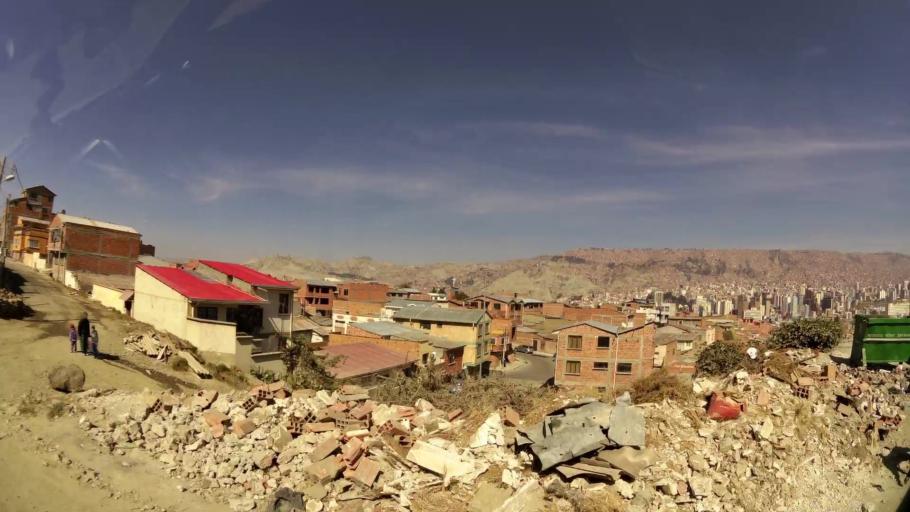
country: BO
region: La Paz
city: La Paz
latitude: -16.5067
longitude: -68.1098
